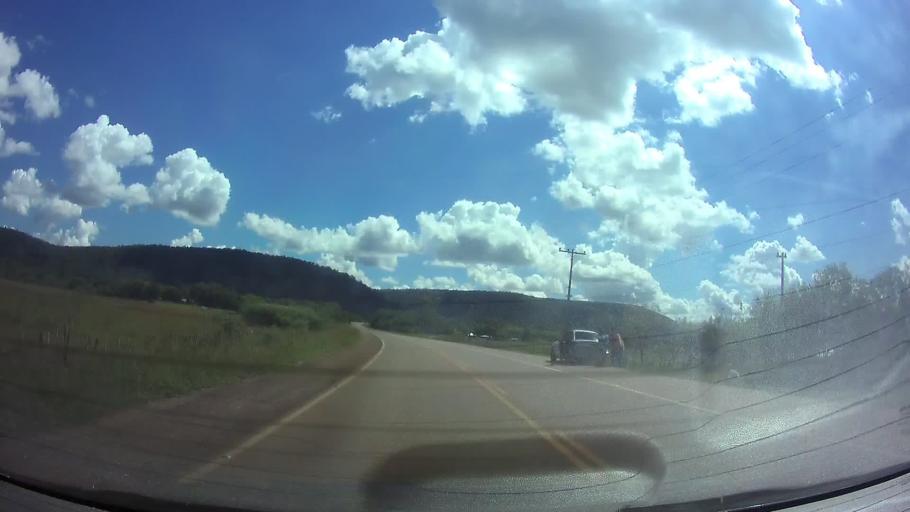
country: PY
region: Paraguari
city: La Colmena
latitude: -25.9143
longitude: -56.7150
